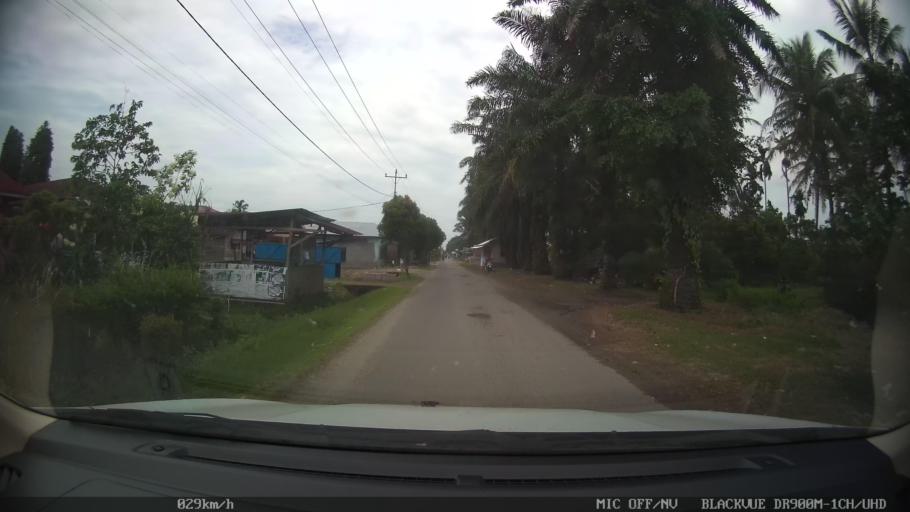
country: ID
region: North Sumatra
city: Sunggal
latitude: 3.6321
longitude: 98.5651
